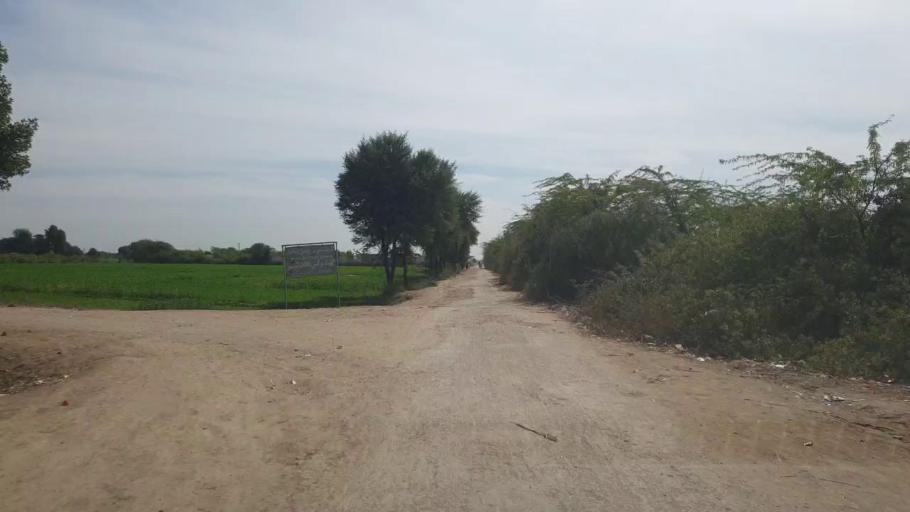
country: PK
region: Sindh
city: Kunri
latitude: 25.3068
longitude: 69.5737
